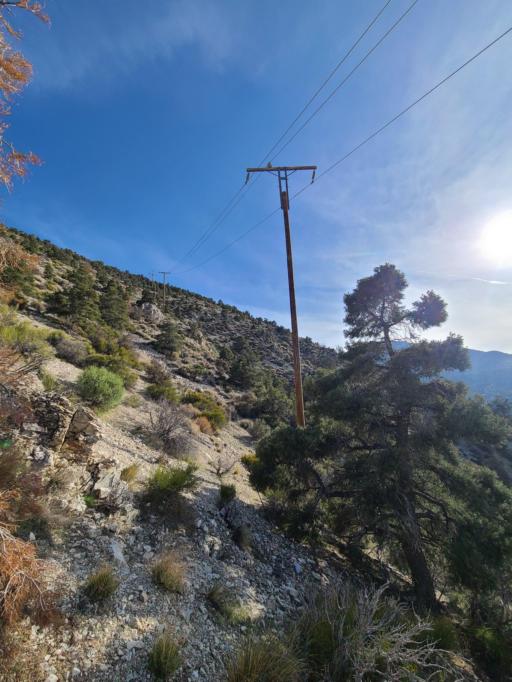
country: US
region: California
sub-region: San Bernardino County
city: Big Bear Lake
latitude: 34.3499
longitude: -116.9134
